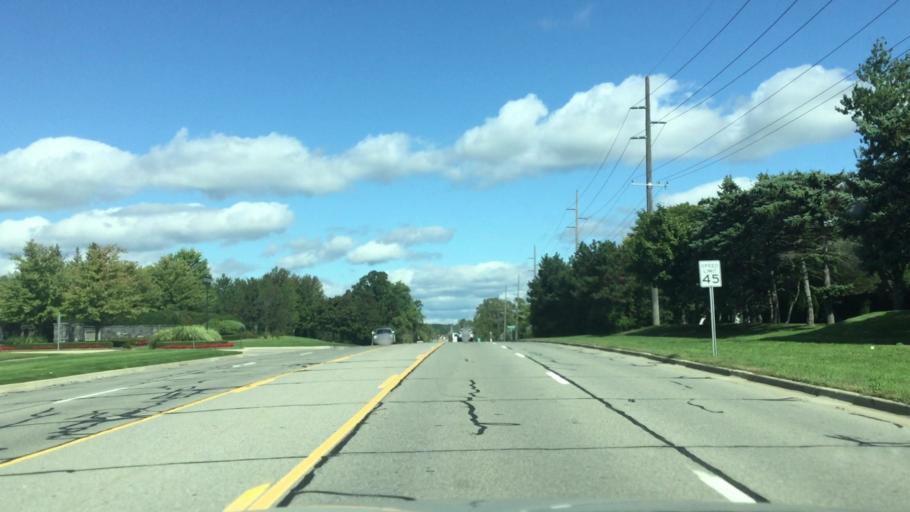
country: US
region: Michigan
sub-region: Oakland County
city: West Bloomfield Township
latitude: 42.5538
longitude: -83.3611
